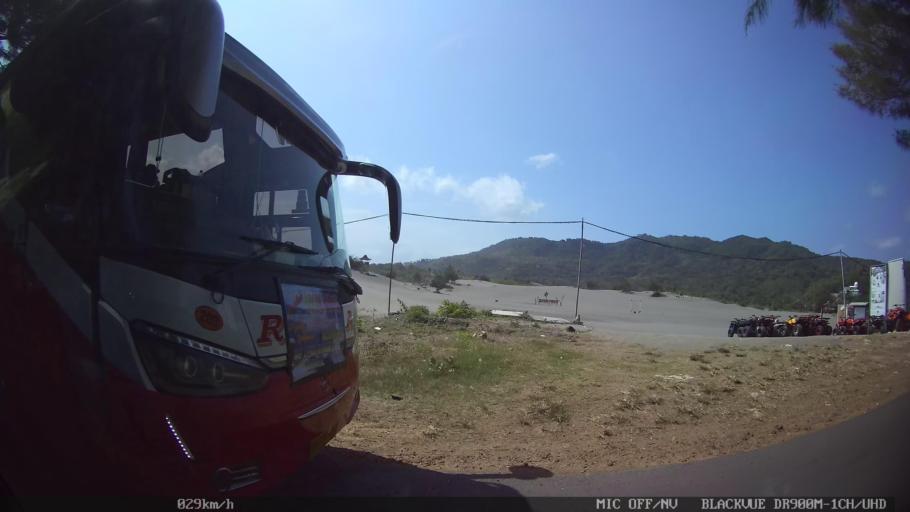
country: ID
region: Daerah Istimewa Yogyakarta
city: Pundong
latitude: -8.0188
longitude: 110.3190
